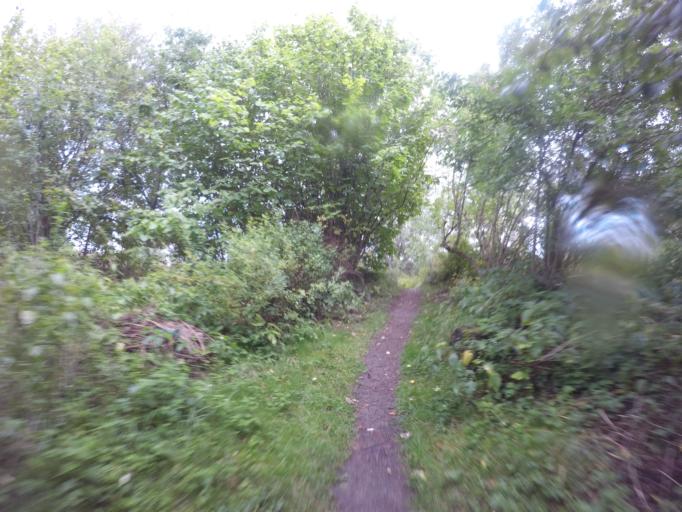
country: SE
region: Vaestmanland
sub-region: Vasteras
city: Vasteras
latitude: 59.6518
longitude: 16.5246
